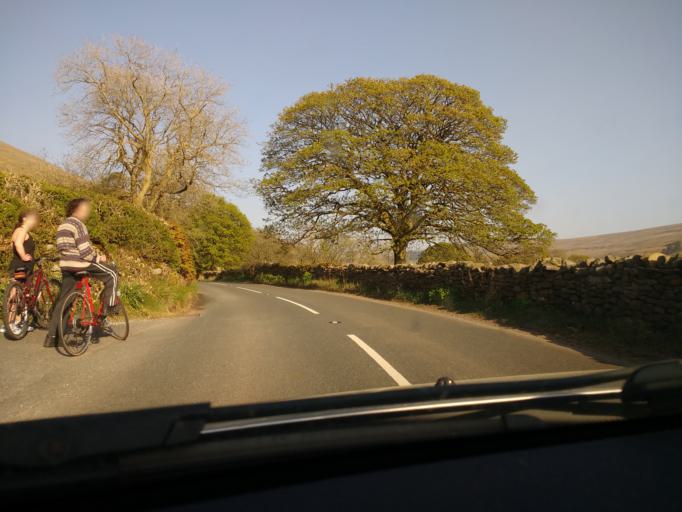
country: GB
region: England
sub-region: Cumbria
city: Sedbergh
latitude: 54.3105
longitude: -2.4301
